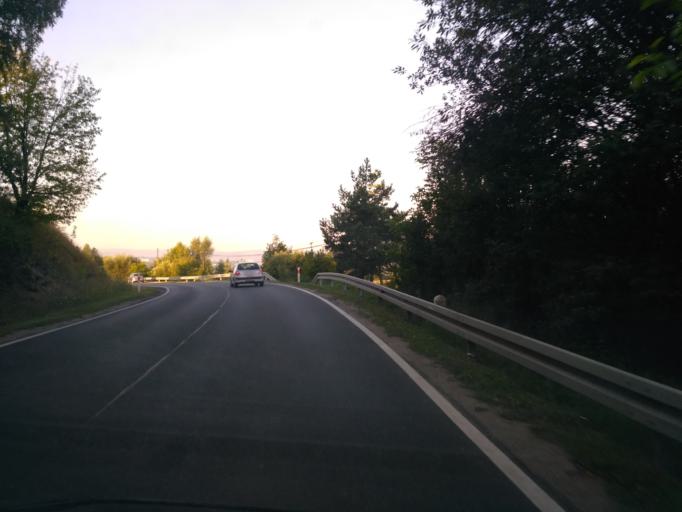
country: PL
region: Subcarpathian Voivodeship
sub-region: Powiat krosnienski
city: Korczyna
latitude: 49.7268
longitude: 21.8099
